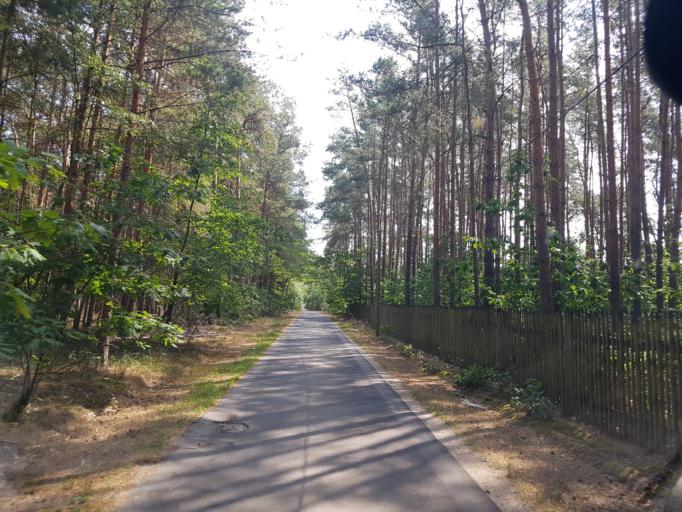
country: DE
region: Brandenburg
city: Finsterwalde
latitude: 51.6602
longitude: 13.7604
